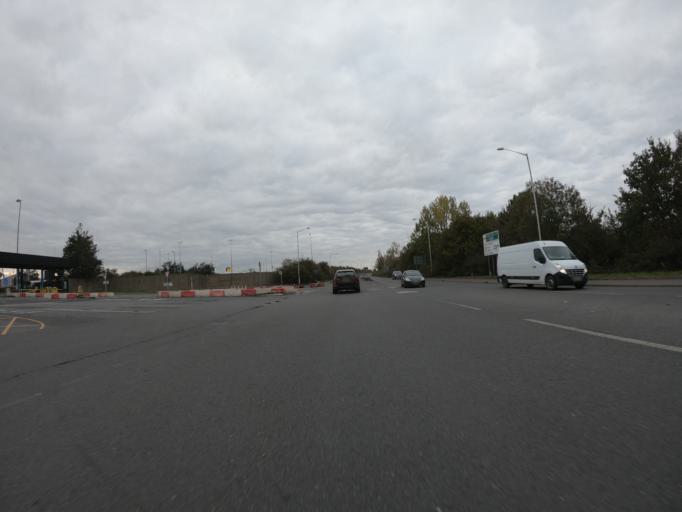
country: GB
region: England
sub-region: Borough of Thurrock
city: Tilbury
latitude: 51.4637
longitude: 0.3505
